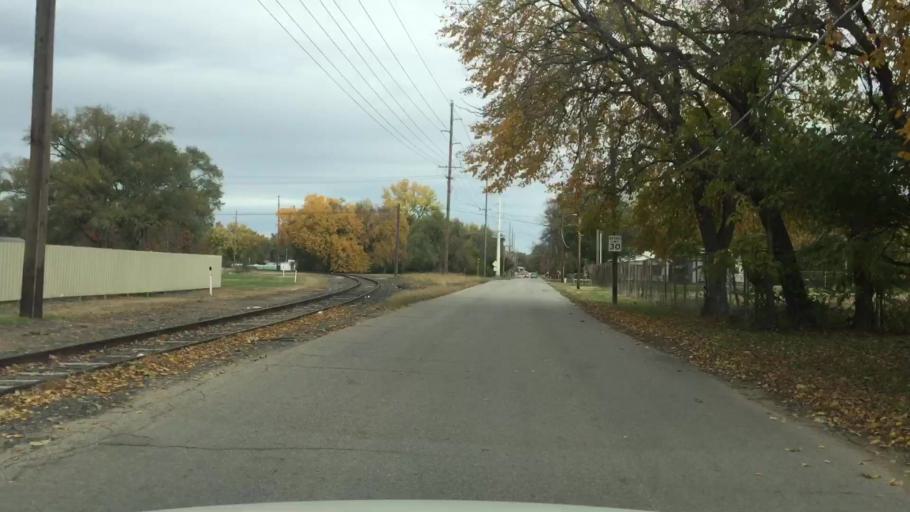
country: US
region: Kansas
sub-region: Shawnee County
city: Topeka
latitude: 39.0726
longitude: -95.6731
